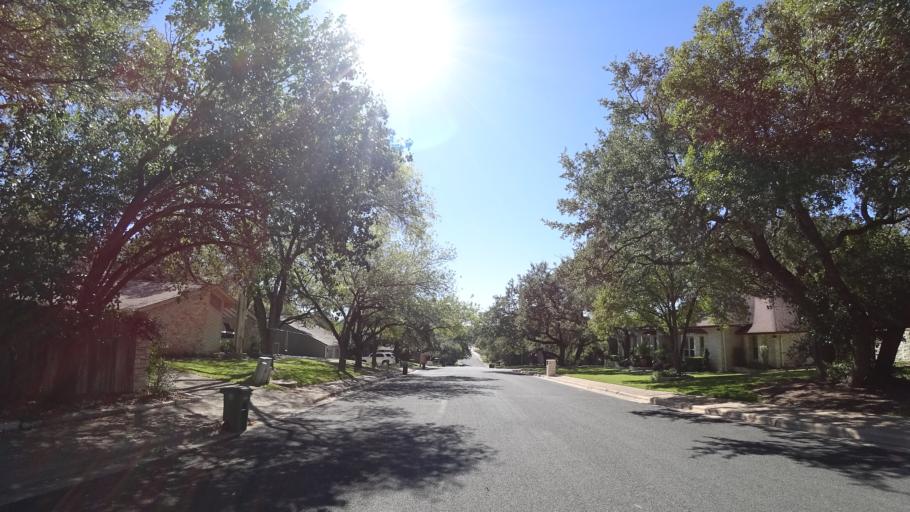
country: US
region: Texas
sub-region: Travis County
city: West Lake Hills
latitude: 30.3635
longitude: -97.7561
